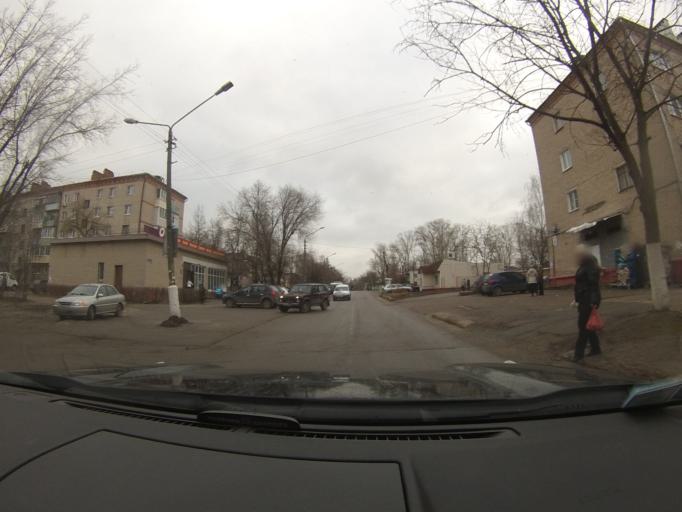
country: RU
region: Moskovskaya
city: Lopatinskiy
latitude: 55.3419
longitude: 38.7252
